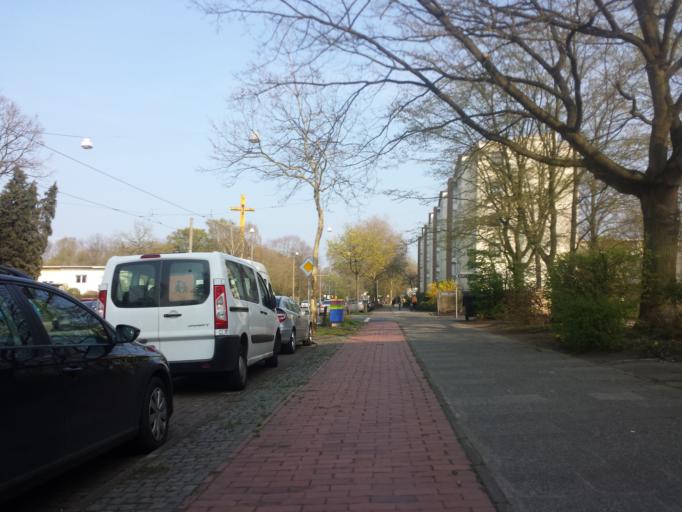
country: DE
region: Lower Saxony
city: Lilienthal
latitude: 53.0783
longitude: 8.9076
